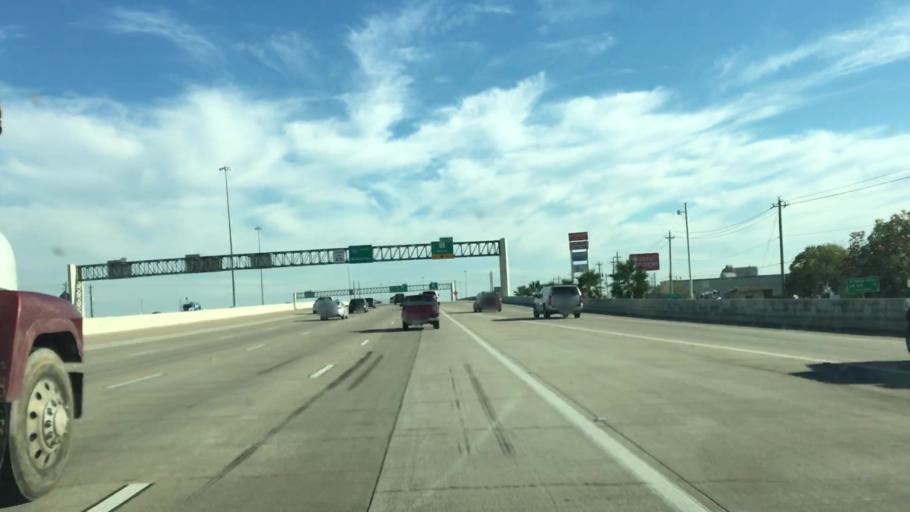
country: US
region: Texas
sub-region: Harris County
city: Webster
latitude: 29.5308
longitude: -95.1332
